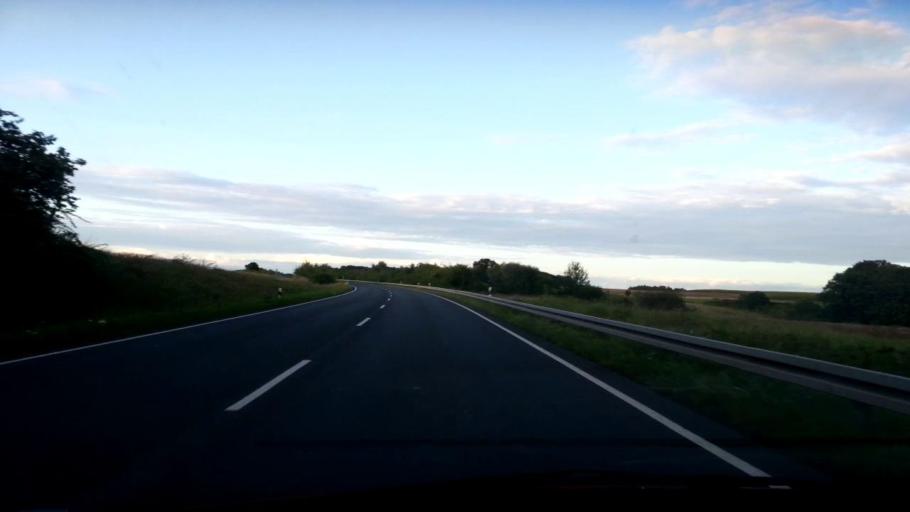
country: DE
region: Bavaria
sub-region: Upper Franconia
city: Stegaurach
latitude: 49.8437
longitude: 10.8412
